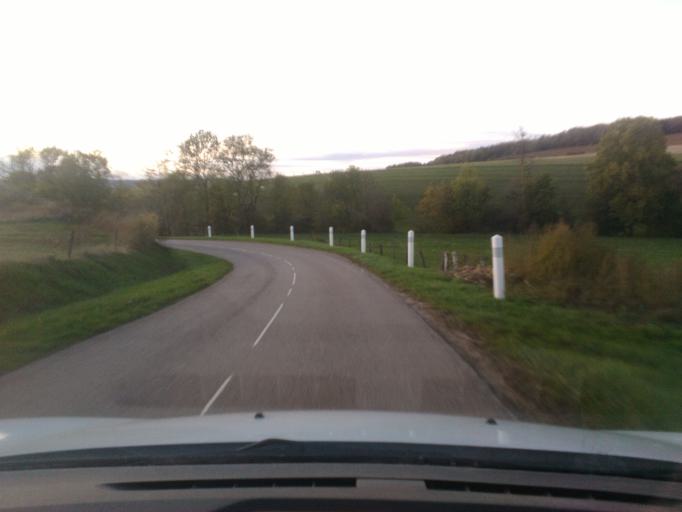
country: FR
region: Lorraine
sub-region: Departement des Vosges
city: Mirecourt
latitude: 48.4004
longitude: 6.1644
